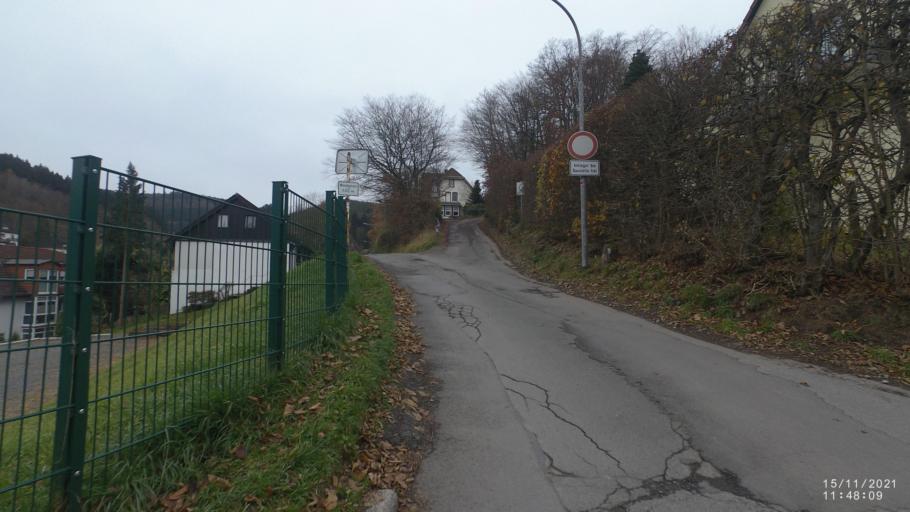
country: DE
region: North Rhine-Westphalia
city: Werdohl
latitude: 51.2337
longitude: 7.7518
